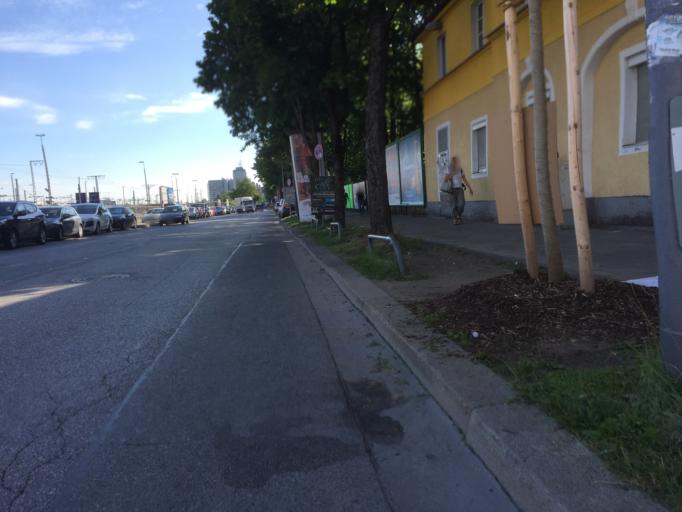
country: DE
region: Bavaria
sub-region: Upper Bavaria
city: Bogenhausen
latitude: 48.1251
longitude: 11.6039
